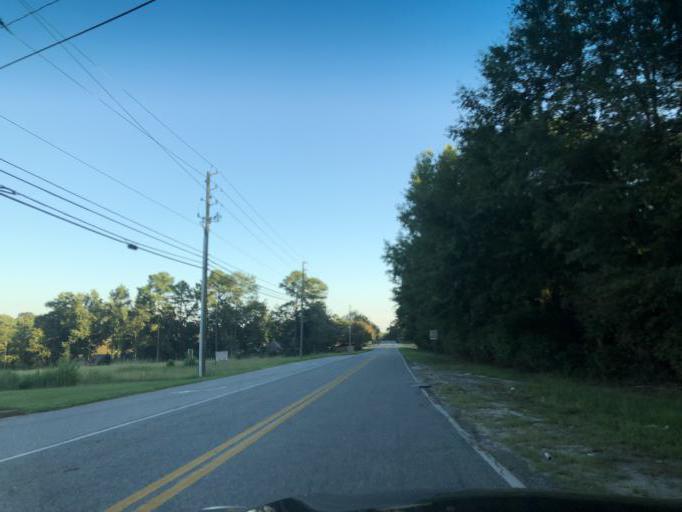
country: US
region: Georgia
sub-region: Muscogee County
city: Columbus
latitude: 32.5429
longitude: -84.8947
